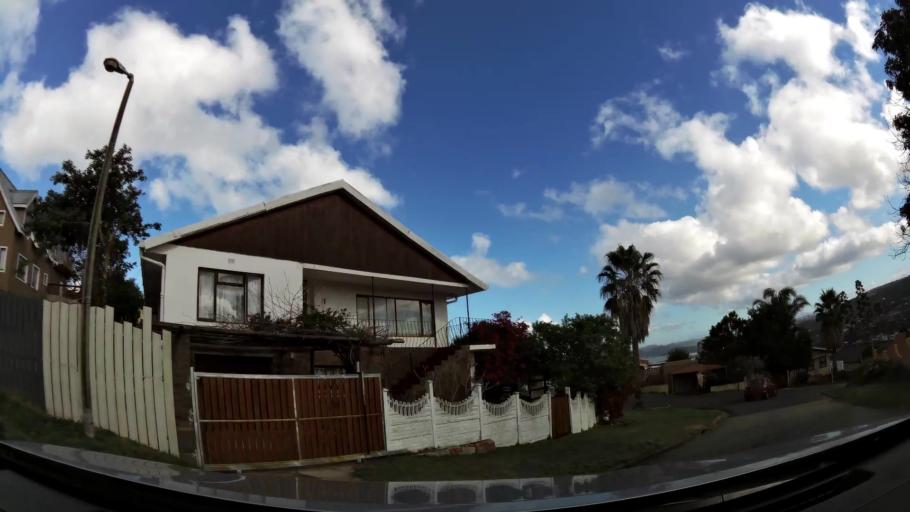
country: ZA
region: Western Cape
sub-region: Eden District Municipality
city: Knysna
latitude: -34.0494
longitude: 23.0849
